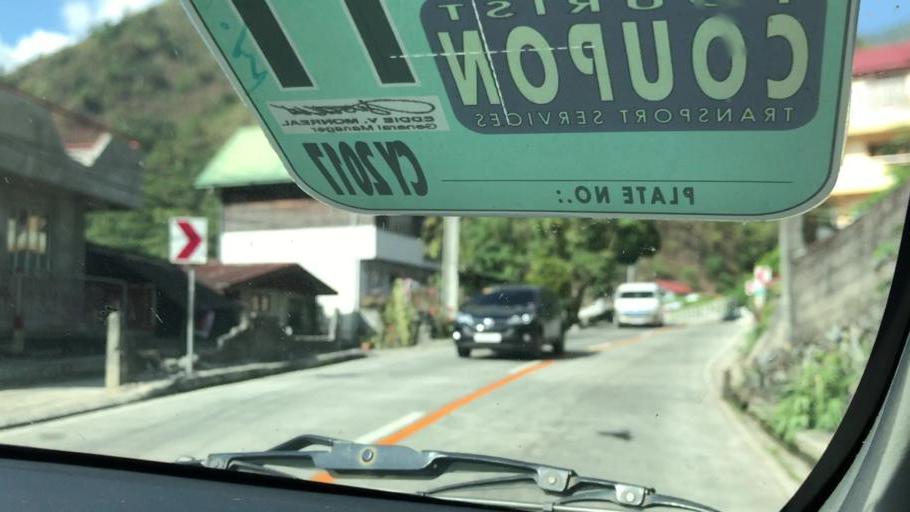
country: PH
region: Cordillera
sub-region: Province of Benguet
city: Tuba
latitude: 16.3155
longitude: 120.6181
